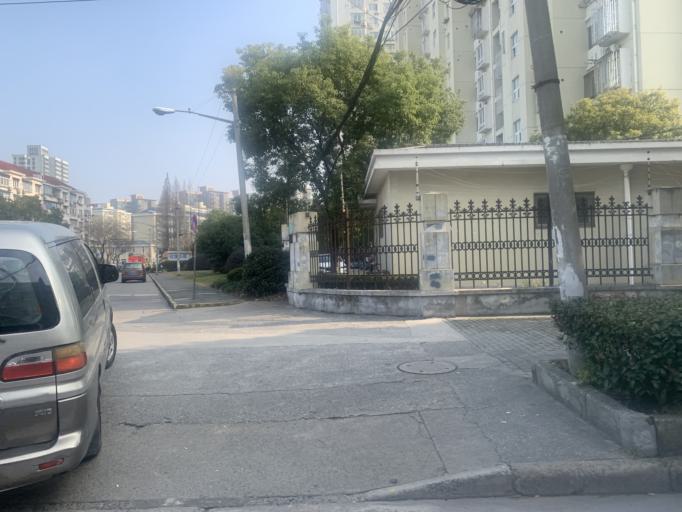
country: CN
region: Shanghai Shi
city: Huamu
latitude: 31.1859
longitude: 121.5145
